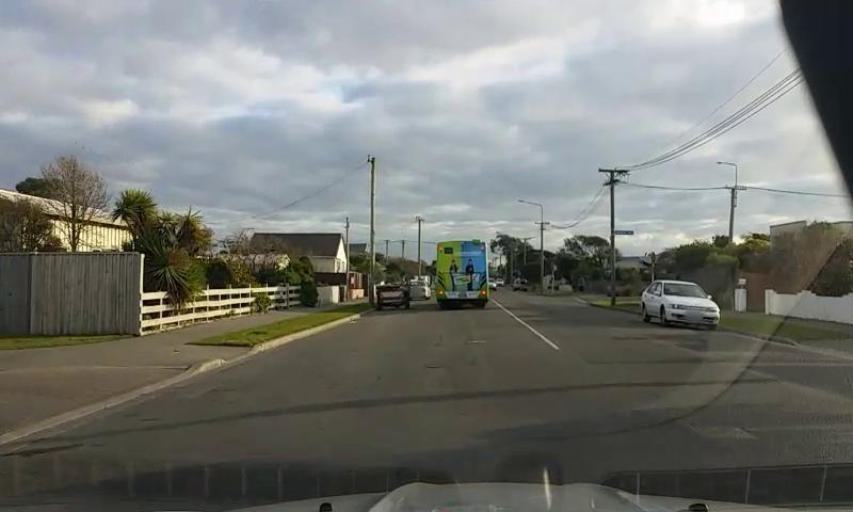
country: NZ
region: Canterbury
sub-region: Christchurch City
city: Christchurch
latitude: -43.5219
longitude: 172.7321
